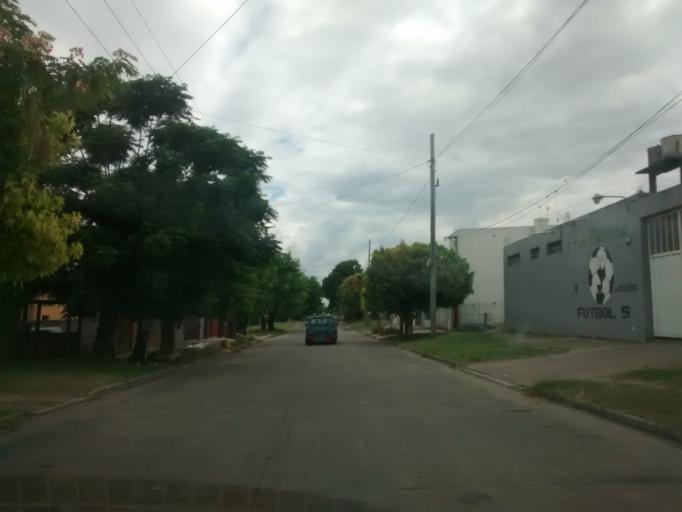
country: AR
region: Buenos Aires
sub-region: Partido de La Plata
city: La Plata
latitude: -34.9227
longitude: -57.9147
